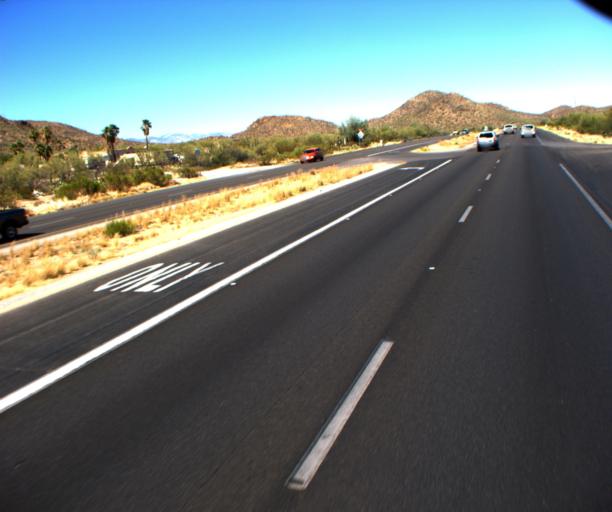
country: US
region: Arizona
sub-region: Pima County
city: Tucson Estates
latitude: 32.1758
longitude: -111.0549
